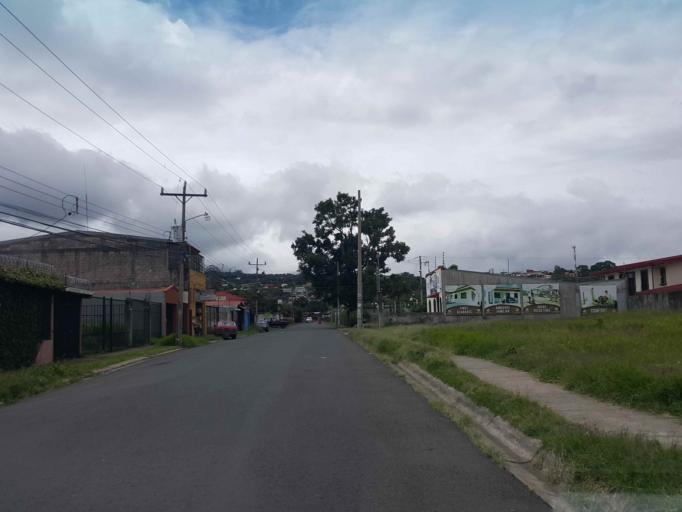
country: CR
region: Heredia
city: Heredia
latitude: 10.0126
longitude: -84.1165
